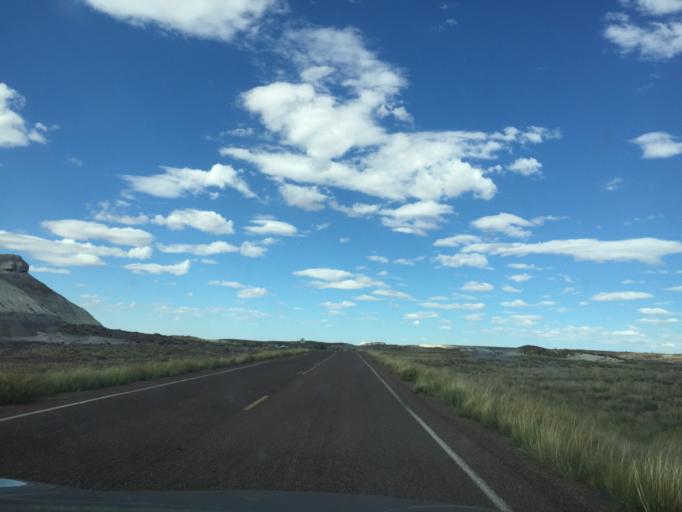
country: US
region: Arizona
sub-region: Navajo County
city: Holbrook
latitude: 34.8615
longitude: -109.7931
